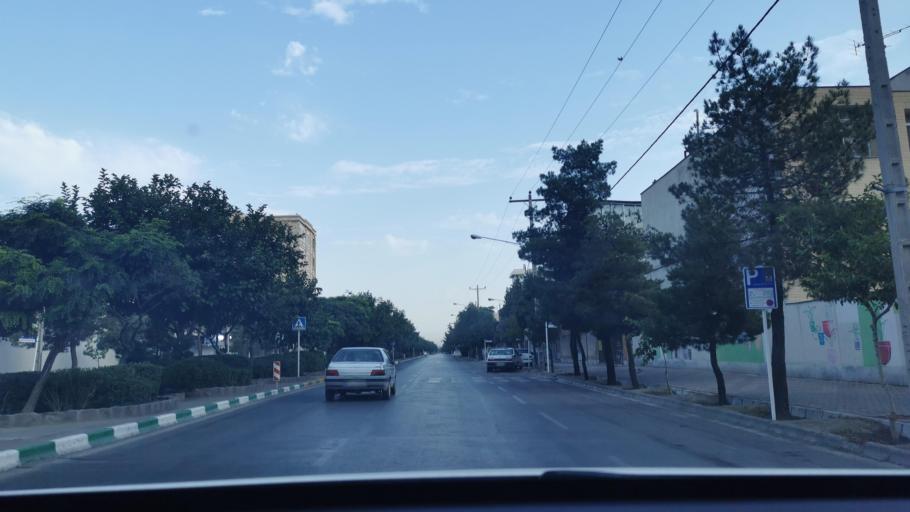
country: IR
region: Razavi Khorasan
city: Mashhad
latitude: 36.3587
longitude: 59.5243
